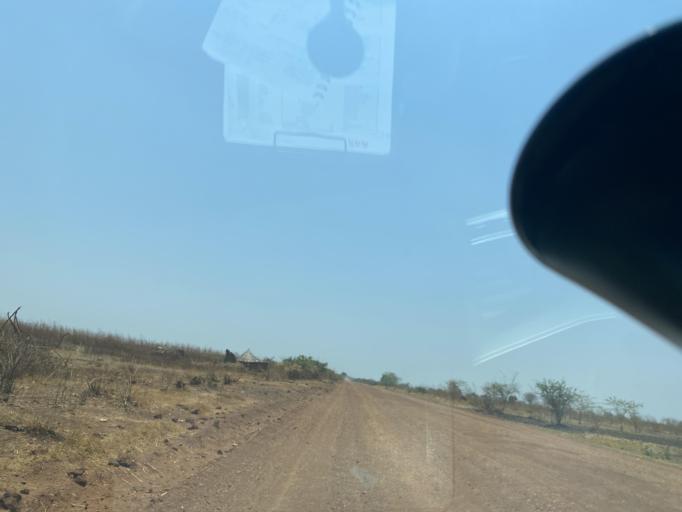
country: ZM
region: Southern
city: Nakambala
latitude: -15.4685
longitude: 27.9049
